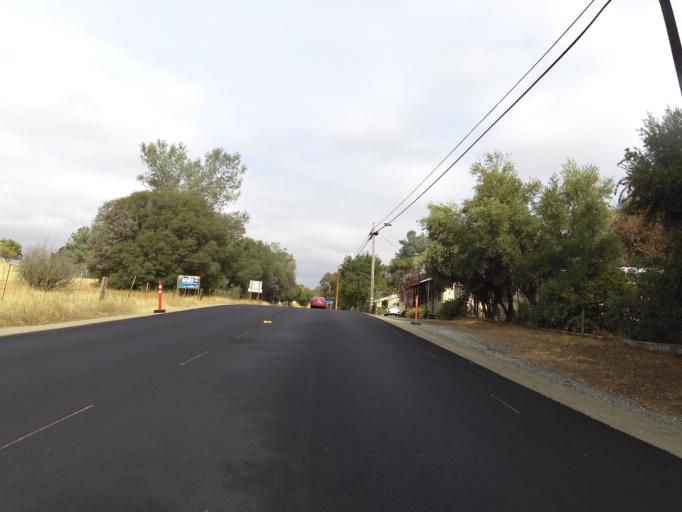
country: US
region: California
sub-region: Calaveras County
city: Angels Camp
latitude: 38.0475
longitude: -120.5279
